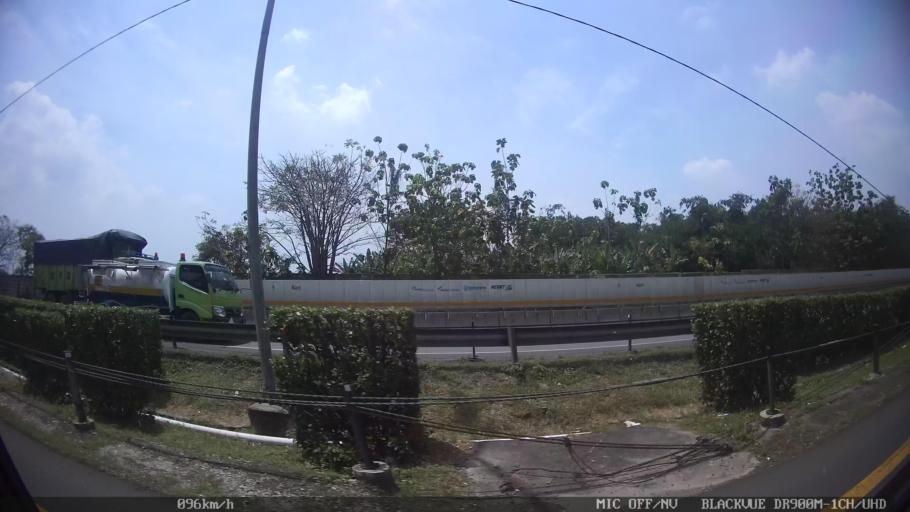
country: ID
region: Banten
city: Serang
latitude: -6.1384
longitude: 106.2286
